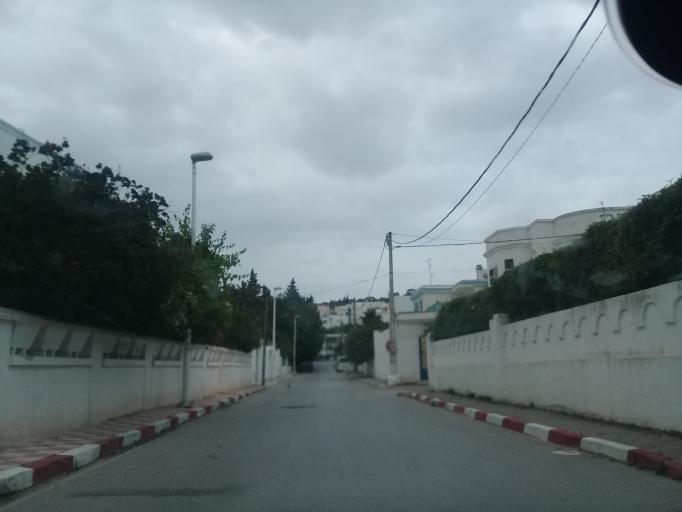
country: TN
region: Tunis
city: Sidi Bou Said
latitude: 36.8701
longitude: 10.3410
